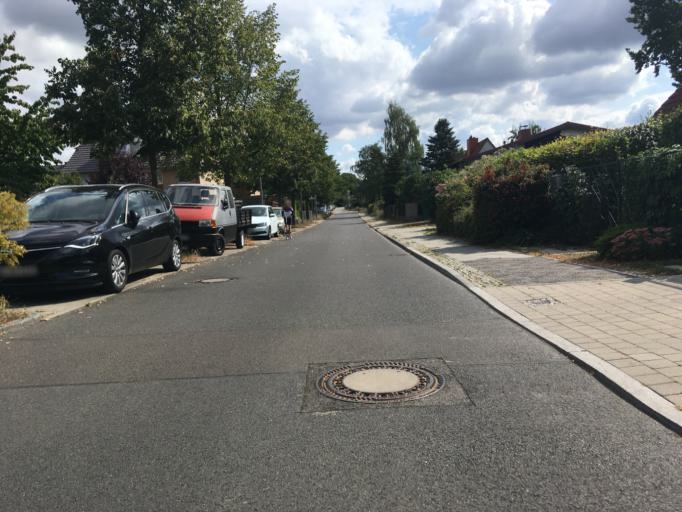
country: DE
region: Berlin
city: Karow
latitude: 52.6110
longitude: 13.4938
